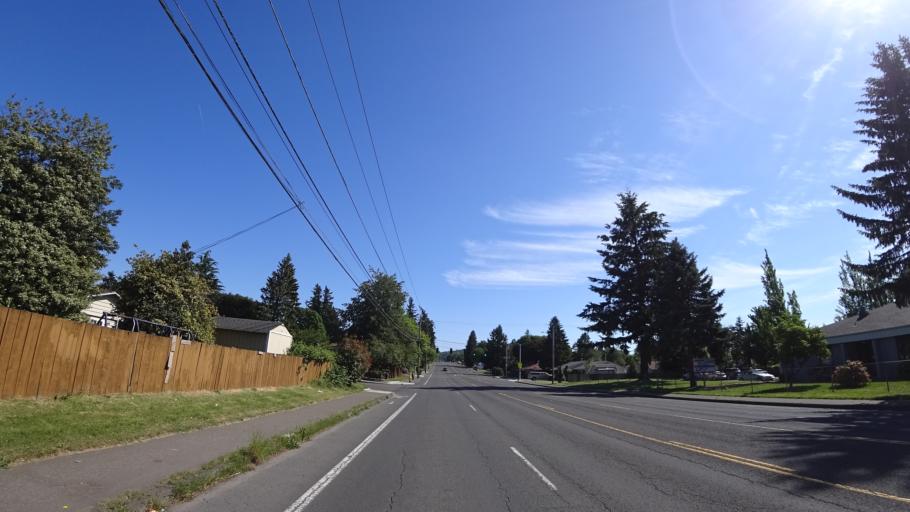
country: US
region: Oregon
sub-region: Multnomah County
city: Gresham
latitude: 45.5015
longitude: -122.4755
